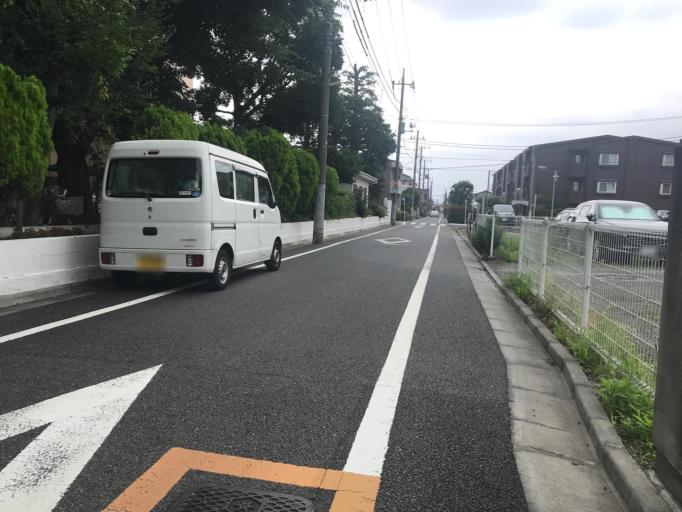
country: JP
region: Saitama
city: Wako
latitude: 35.7294
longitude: 139.6183
